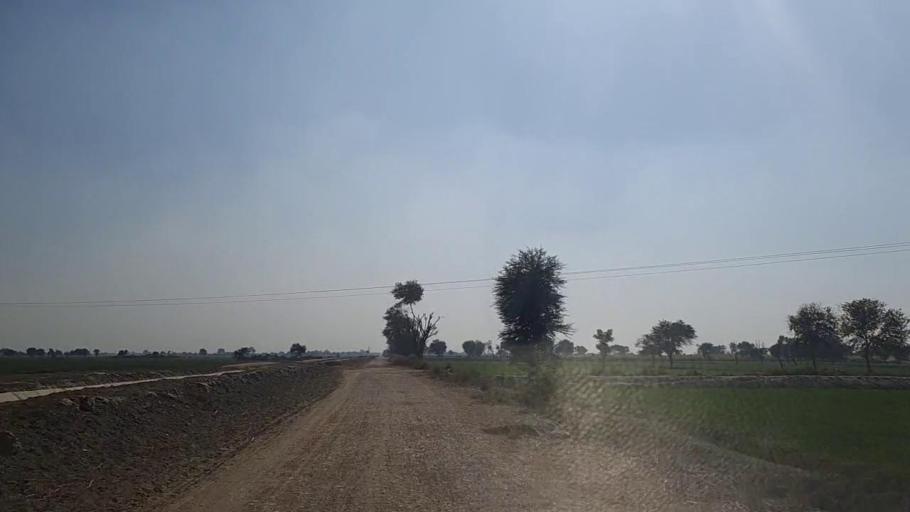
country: PK
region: Sindh
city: Shahpur Chakar
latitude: 26.2055
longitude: 68.5838
